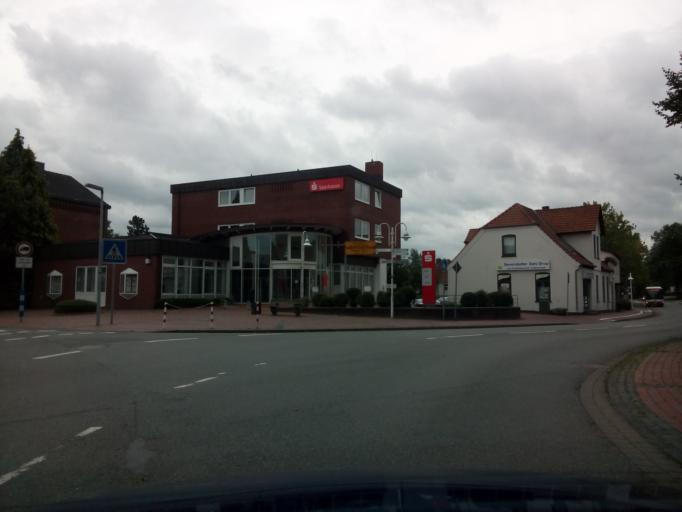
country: DE
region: Lower Saxony
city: Beverstedt
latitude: 53.4343
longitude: 8.8191
